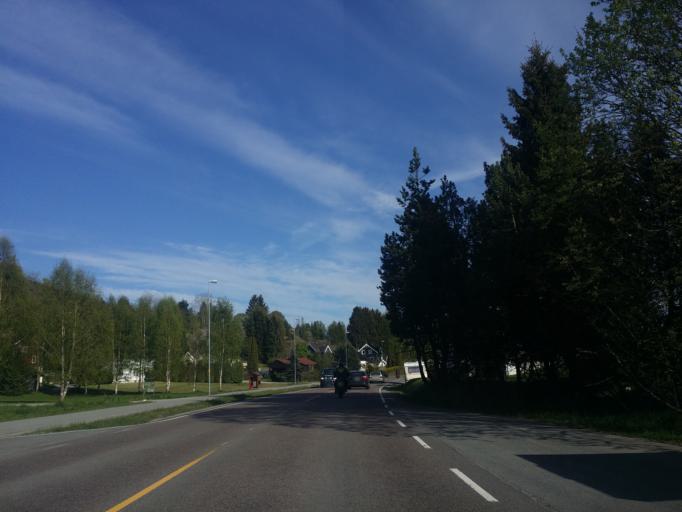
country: NO
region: Telemark
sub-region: Notodden
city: Notodden
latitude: 59.5755
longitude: 9.1939
